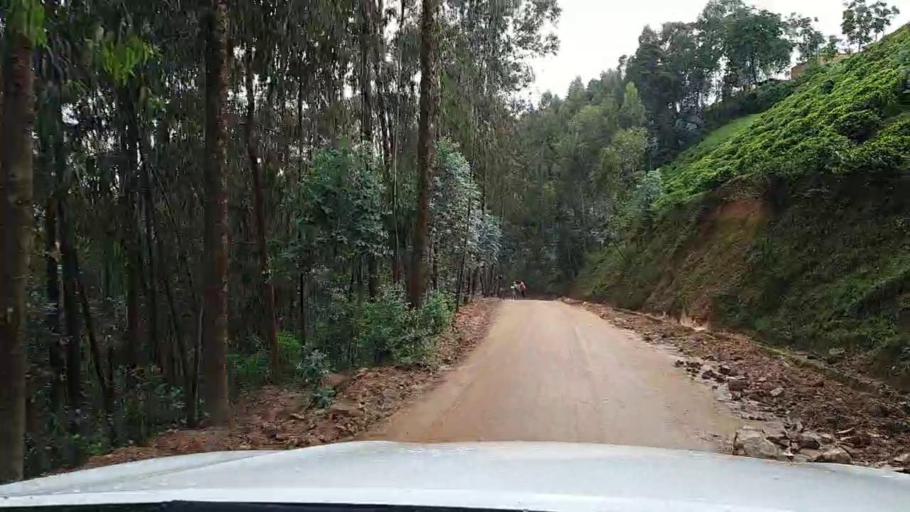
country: RW
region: Southern Province
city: Nzega
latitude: -2.4579
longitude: 29.4662
